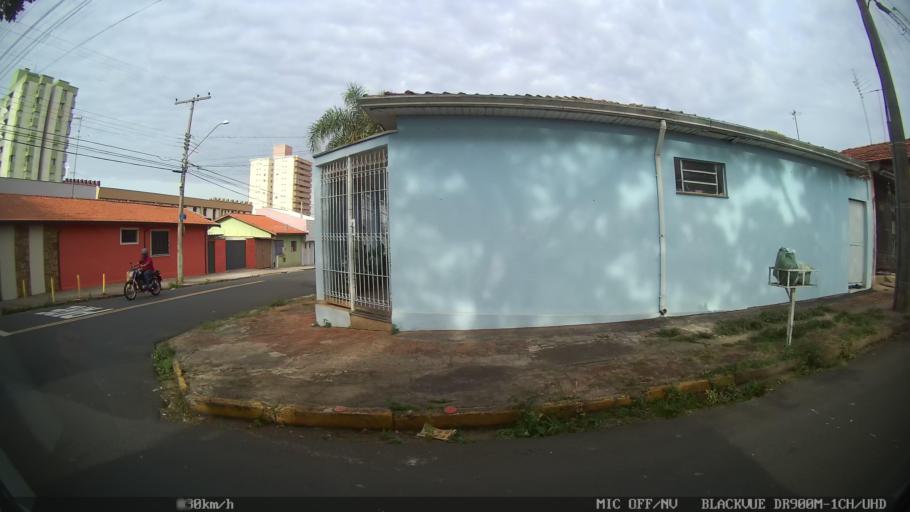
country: BR
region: Sao Paulo
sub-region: Piracicaba
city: Piracicaba
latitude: -22.7298
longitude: -47.6330
